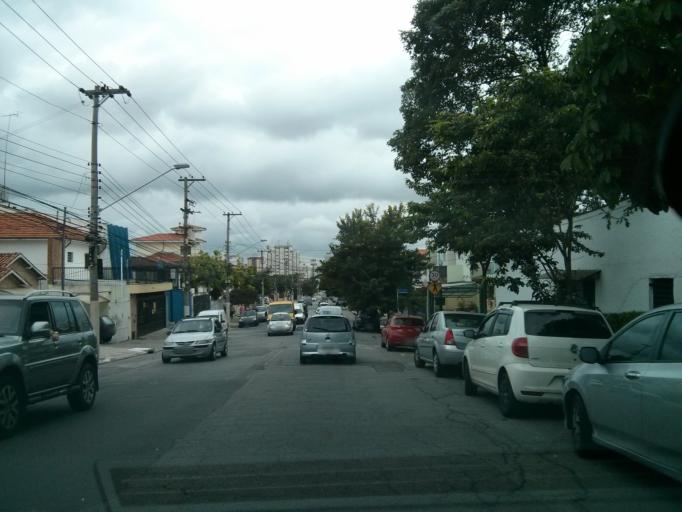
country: BR
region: Sao Paulo
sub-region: Sao Paulo
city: Sao Paulo
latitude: -23.6042
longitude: -46.6349
